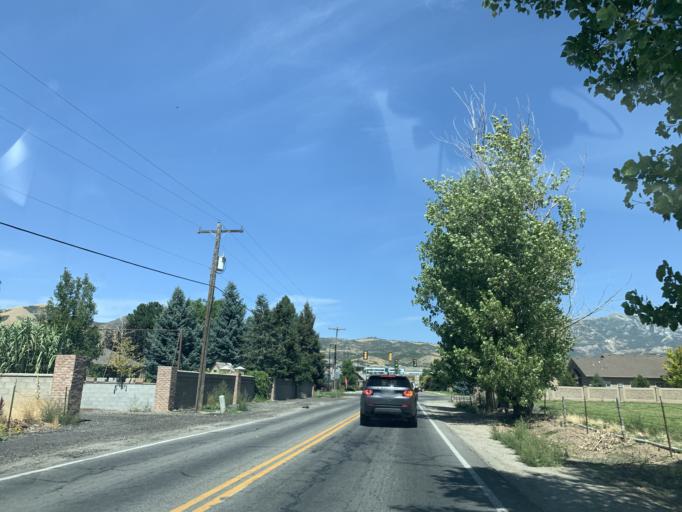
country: US
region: Utah
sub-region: Utah County
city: Lehi
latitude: 40.4272
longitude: -111.8305
